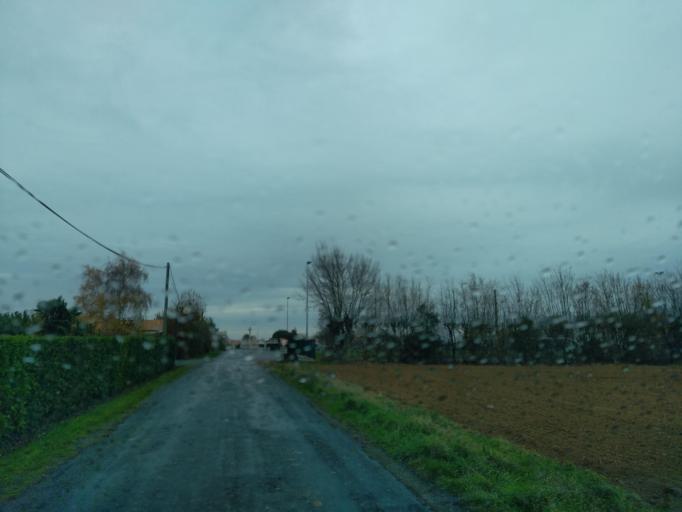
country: FR
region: Pays de la Loire
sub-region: Departement de la Vendee
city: Maillezais
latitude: 46.3689
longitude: -0.7347
